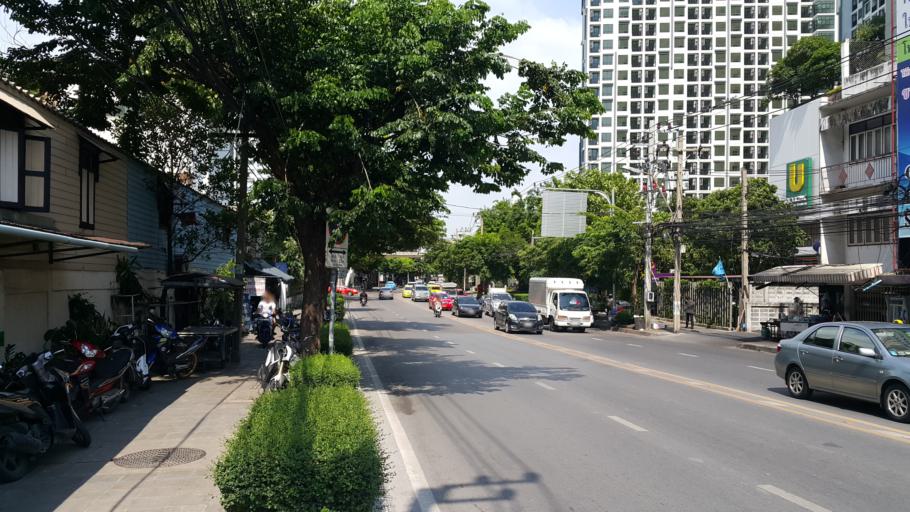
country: TH
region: Bangkok
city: Phra Khanong
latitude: 13.7111
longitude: 100.6032
